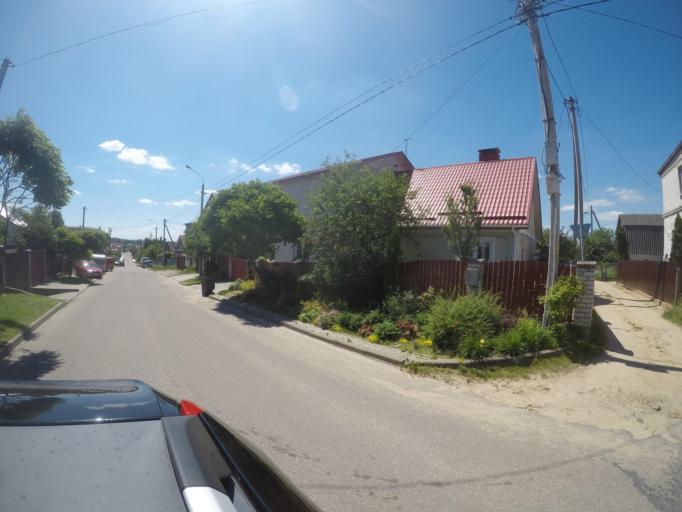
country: BY
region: Grodnenskaya
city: Hrodna
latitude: 53.6921
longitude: 23.8178
